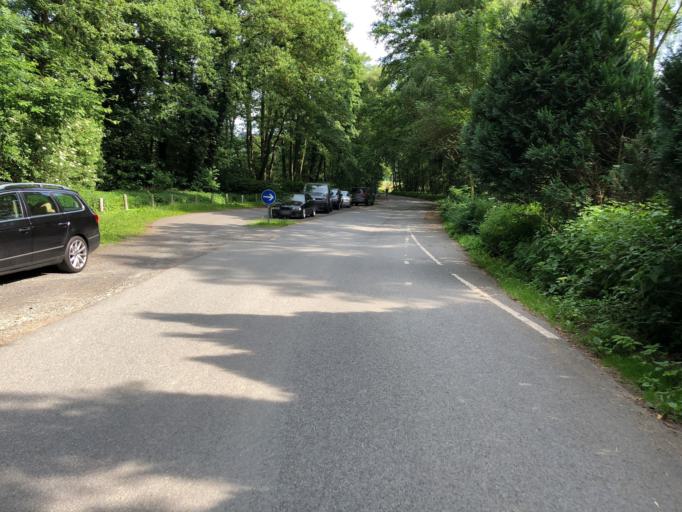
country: DE
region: Hesse
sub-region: Regierungsbezirk Darmstadt
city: Konigstein im Taunus
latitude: 50.1819
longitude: 8.4547
